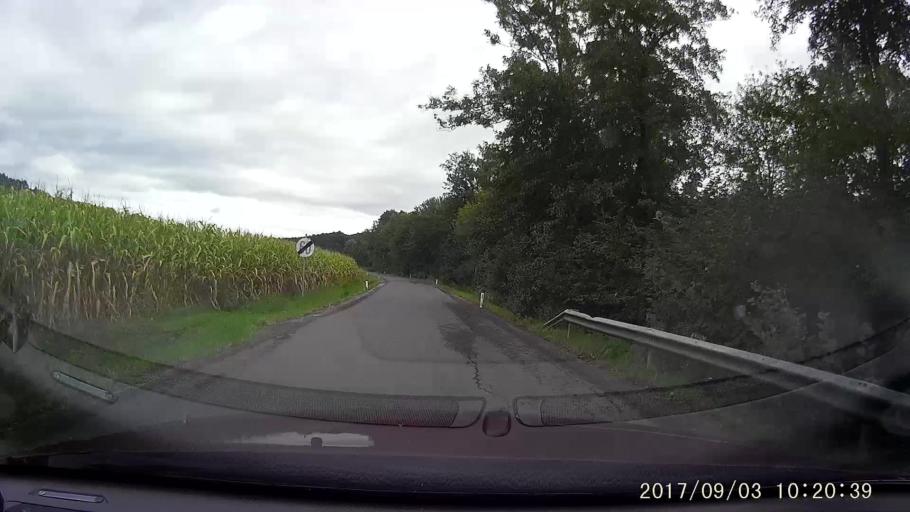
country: AT
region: Styria
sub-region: Politischer Bezirk Suedoststeiermark
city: Breitenfeld an der Rittschein
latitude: 47.0350
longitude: 15.9140
